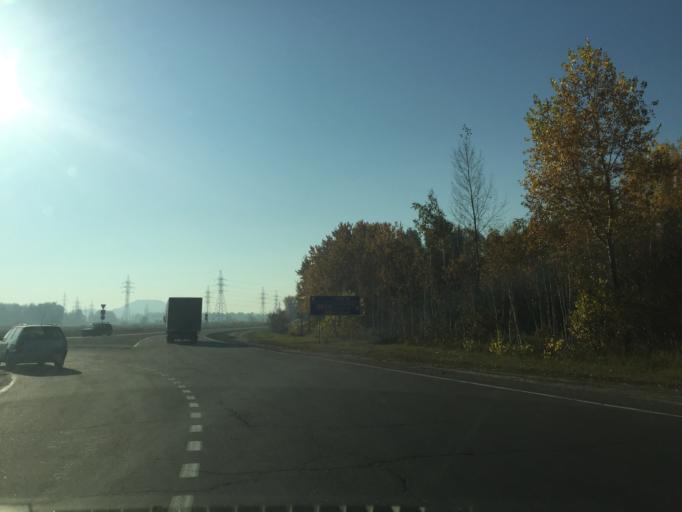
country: BY
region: Gomel
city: Kastsyukowka
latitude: 52.4527
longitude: 30.8245
